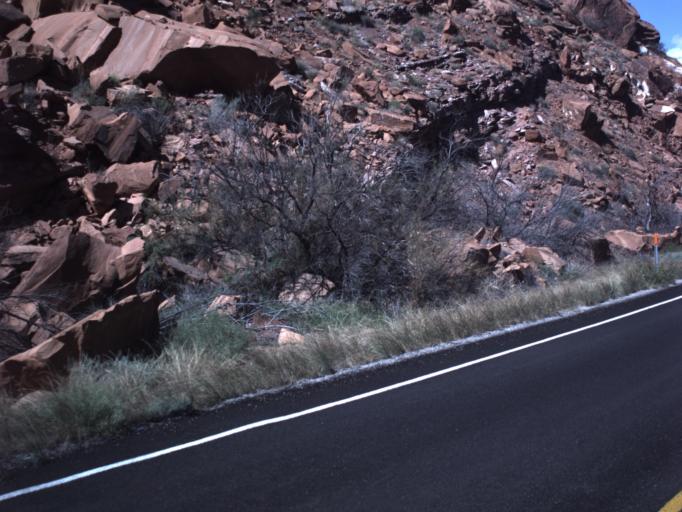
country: US
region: Utah
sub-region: Grand County
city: Moab
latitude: 38.5712
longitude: -109.5804
